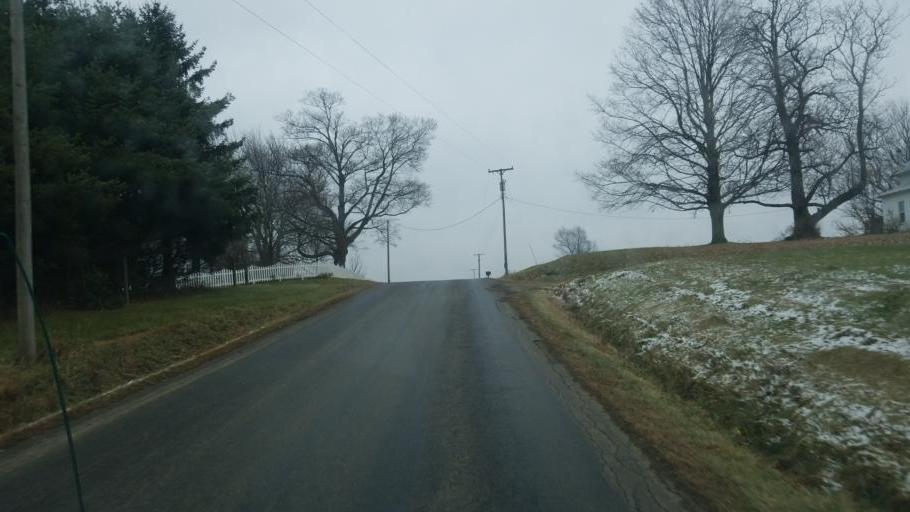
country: US
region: Ohio
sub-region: Huron County
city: Greenwich
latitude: 40.9756
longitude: -82.5230
